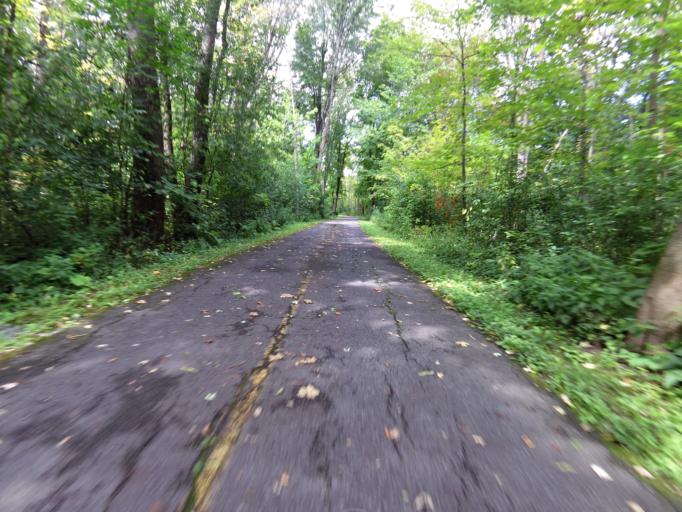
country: CA
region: Ontario
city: Ottawa
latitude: 45.4459
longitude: -75.6421
